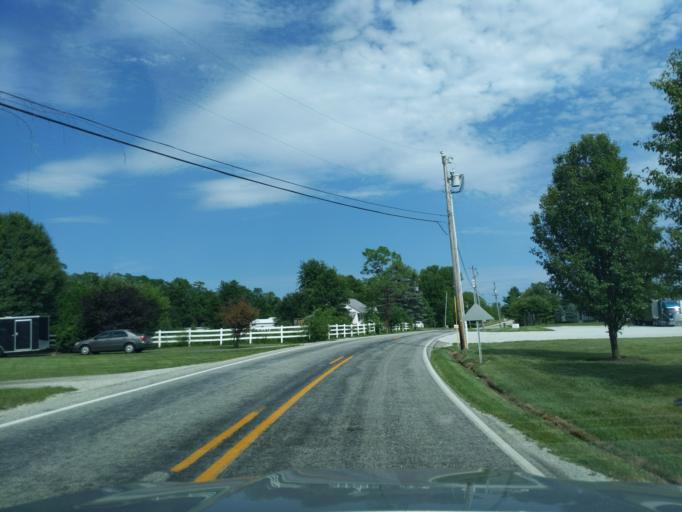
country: US
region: Indiana
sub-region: Ripley County
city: Osgood
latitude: 39.2049
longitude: -85.3217
